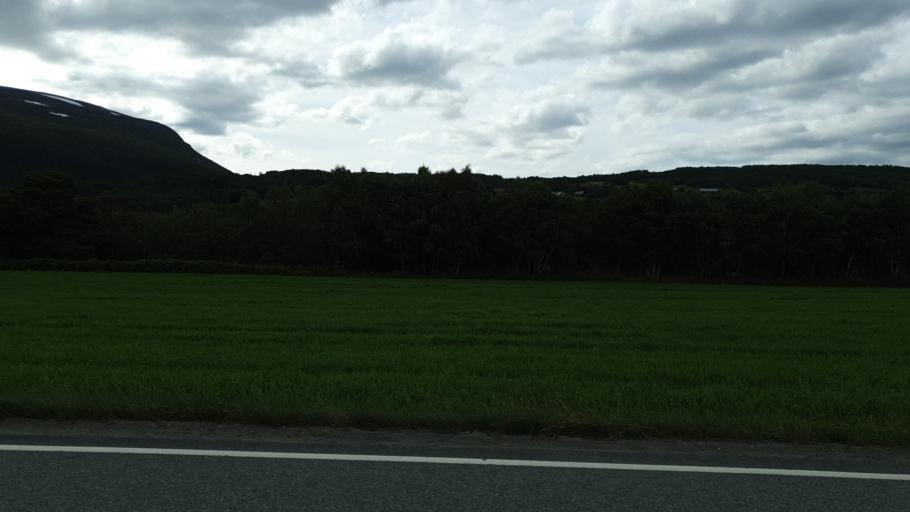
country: NO
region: Sor-Trondelag
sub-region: Oppdal
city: Oppdal
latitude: 62.5588
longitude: 9.6372
